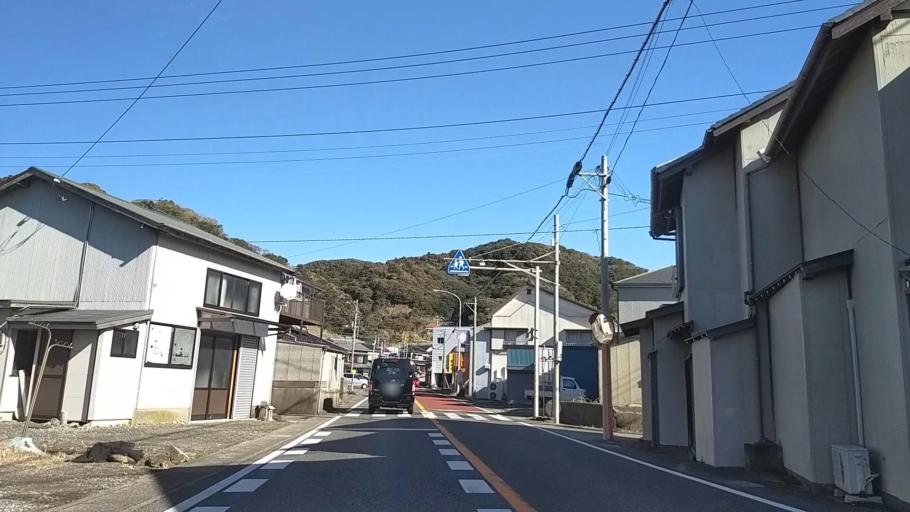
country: JP
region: Chiba
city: Kawaguchi
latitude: 35.0363
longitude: 140.0105
